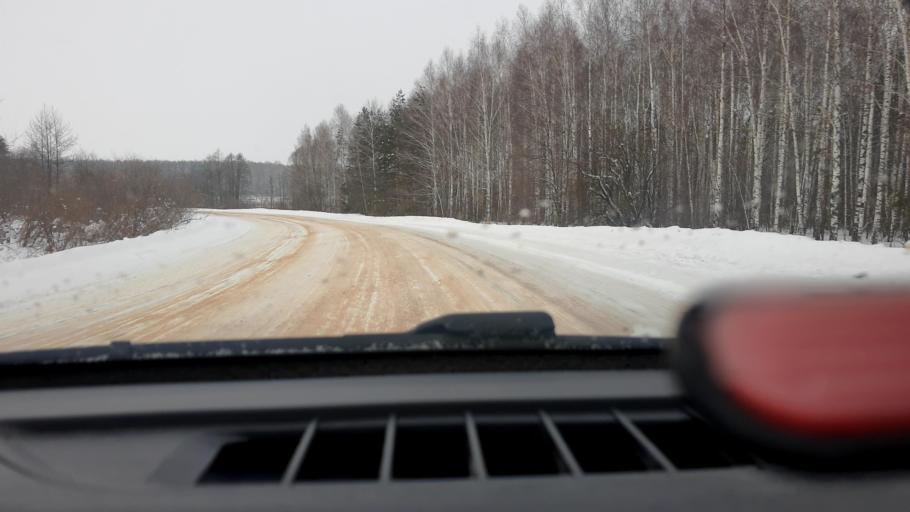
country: RU
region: Nizjnij Novgorod
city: Buturlino
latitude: 55.5932
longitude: 44.9196
